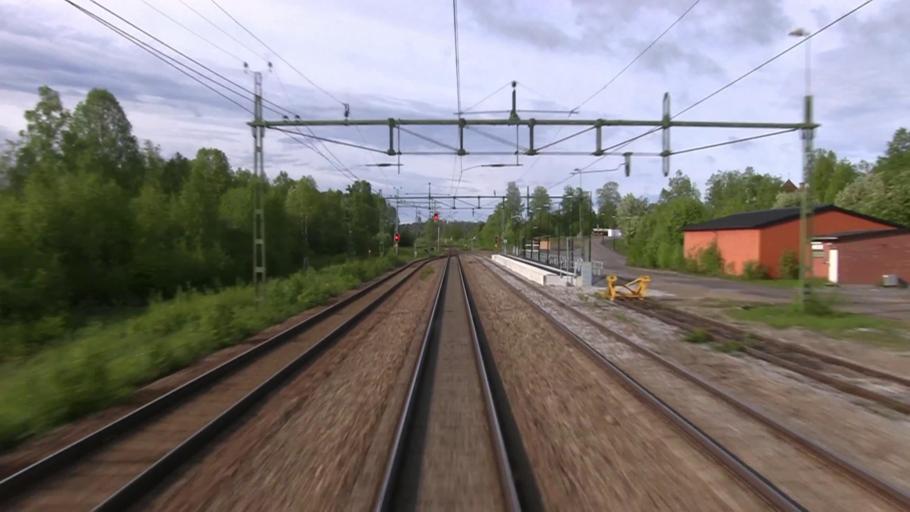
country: SE
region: Vaesterbotten
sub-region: Vindelns Kommun
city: Vindeln
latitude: 64.0983
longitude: 19.6761
